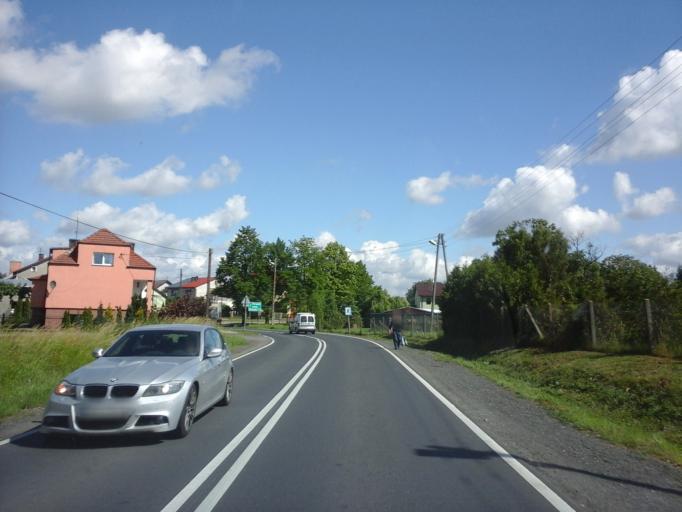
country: PL
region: West Pomeranian Voivodeship
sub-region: Powiat lobeski
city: Wegorzyno
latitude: 53.5314
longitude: 15.5612
